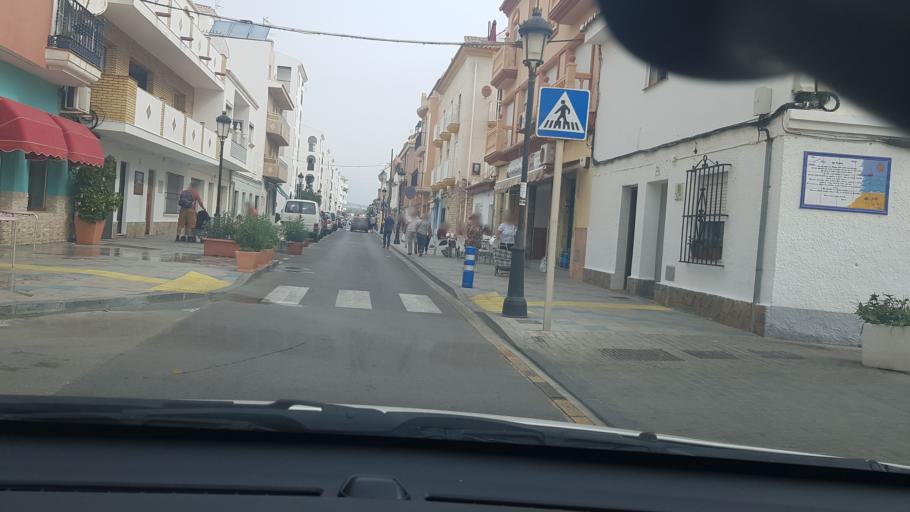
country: ES
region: Andalusia
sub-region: Provincia de Malaga
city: Manilva
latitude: 36.3673
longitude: -5.2253
